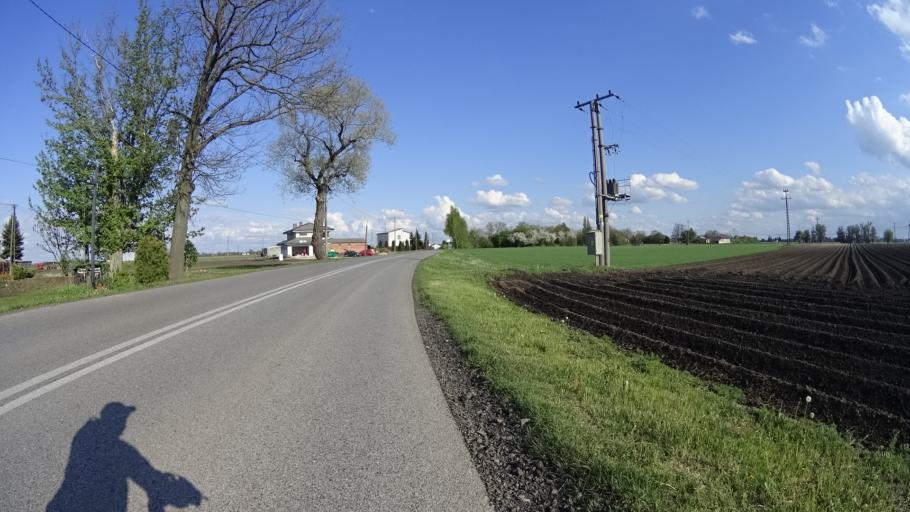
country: PL
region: Masovian Voivodeship
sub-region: Powiat warszawski zachodni
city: Jozefow
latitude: 52.2341
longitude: 20.7289
